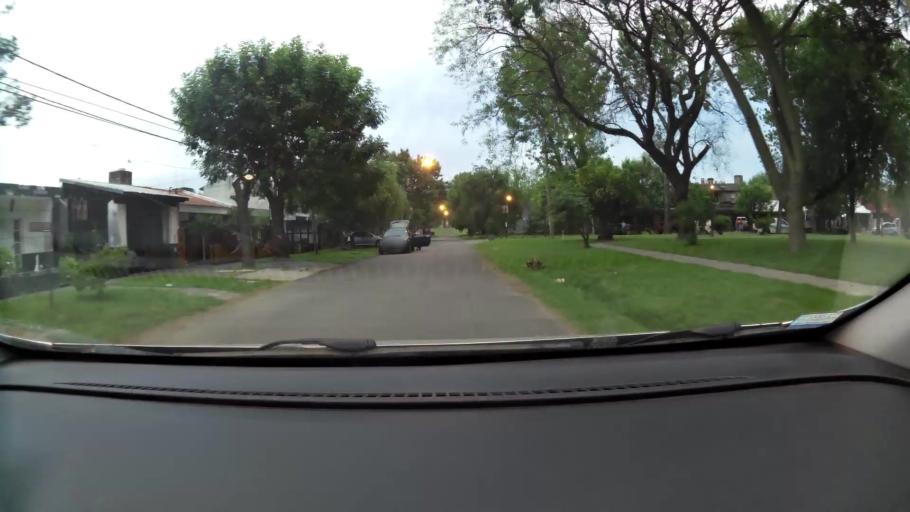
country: AR
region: Santa Fe
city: Granadero Baigorria
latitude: -32.8783
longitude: -60.7057
